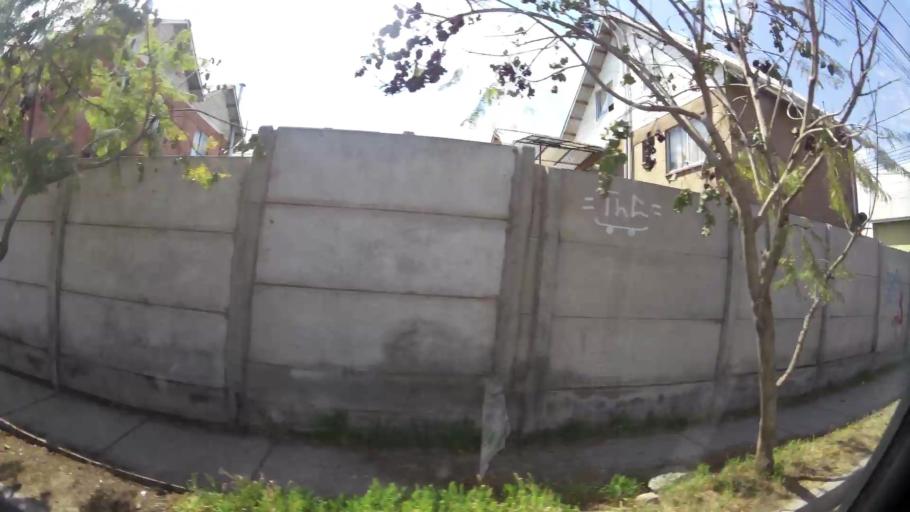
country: CL
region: Santiago Metropolitan
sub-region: Provincia de Talagante
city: Talagante
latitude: -33.6638
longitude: -70.9166
